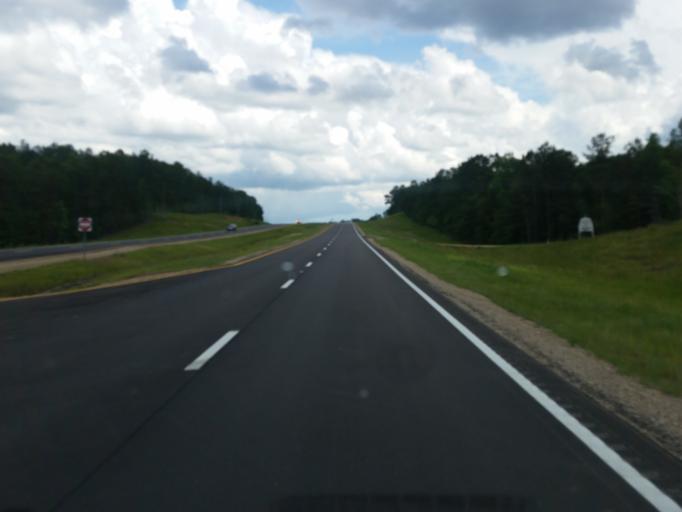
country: US
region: Mississippi
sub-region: George County
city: Lucedale
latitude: 31.0595
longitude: -88.7337
